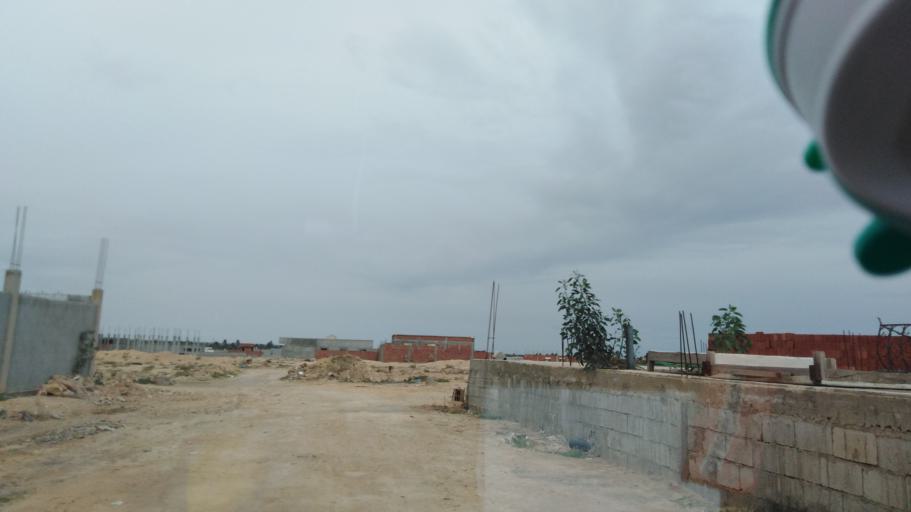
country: TN
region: Qabis
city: Gabes
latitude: 33.9520
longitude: 10.0058
